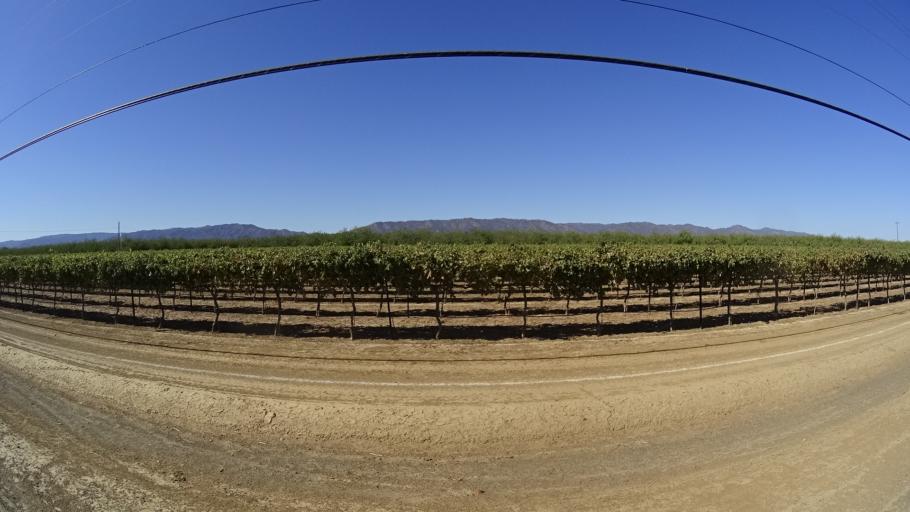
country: US
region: California
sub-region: Yolo County
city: Winters
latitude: 38.5411
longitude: -121.9712
